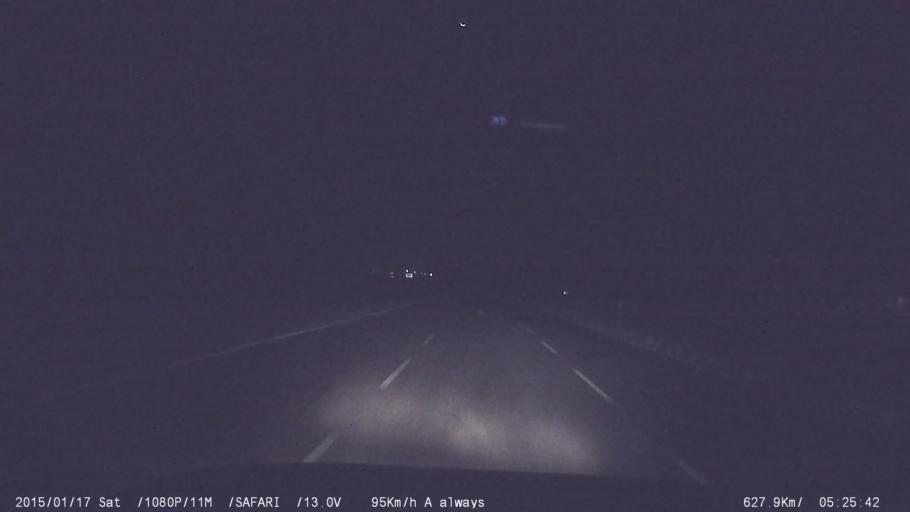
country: IN
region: Tamil Nadu
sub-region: Vellore
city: Arcot
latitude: 12.9412
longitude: 79.2365
